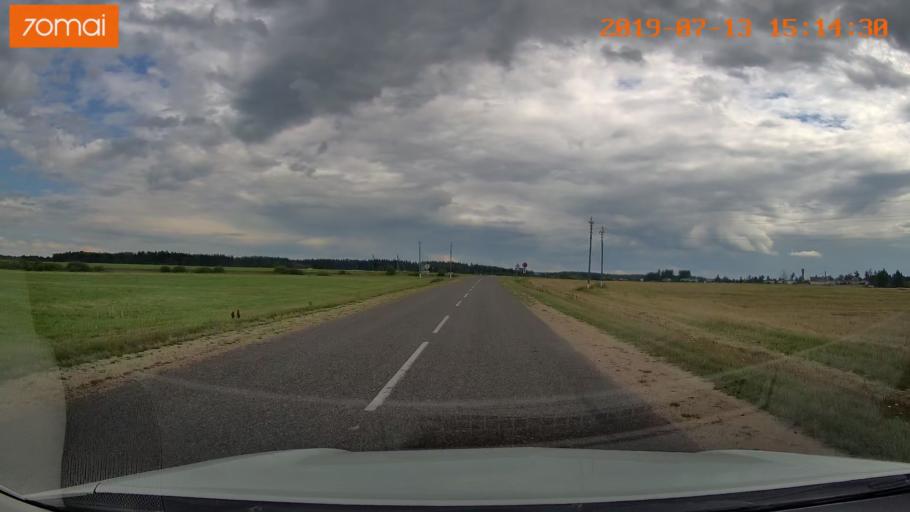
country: BY
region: Mogilev
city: Hlusha
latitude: 53.1266
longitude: 28.8197
